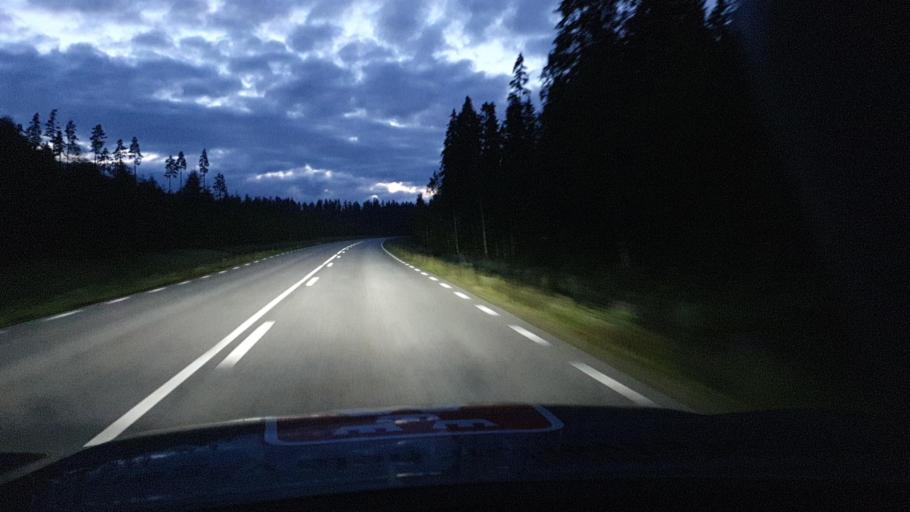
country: SE
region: OErebro
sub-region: Karlskoga Kommun
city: Karlskoga
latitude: 59.4003
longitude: 14.5132
